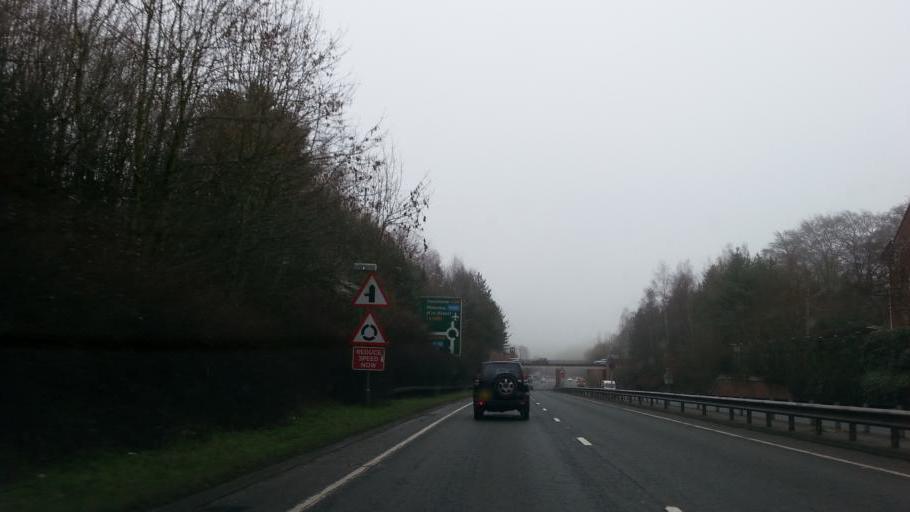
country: GB
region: England
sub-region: Cheshire East
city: Wilmslow
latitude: 53.3241
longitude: -2.2258
